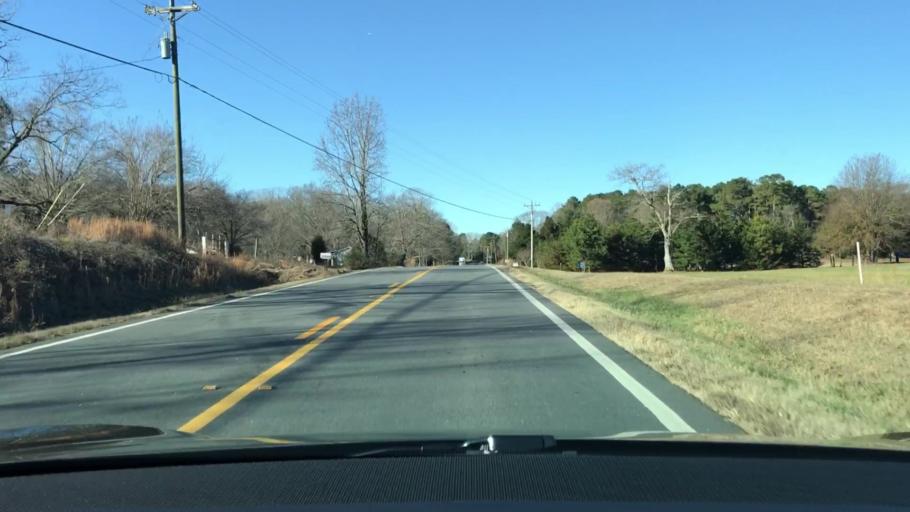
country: US
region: Georgia
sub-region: Barrow County
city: Auburn
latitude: 33.9866
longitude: -83.7979
